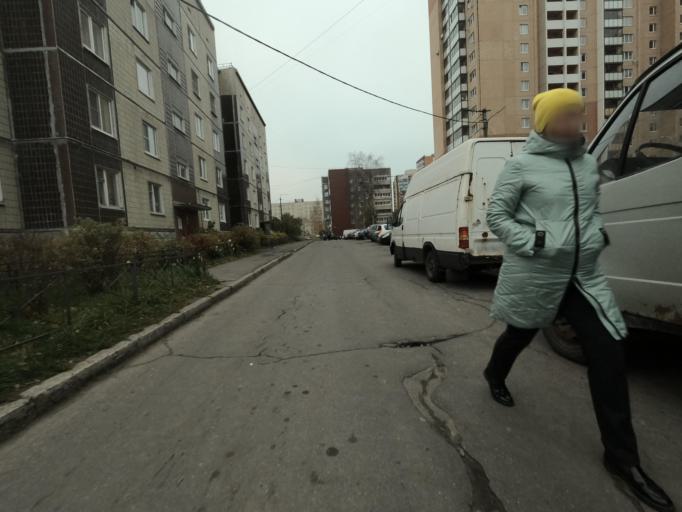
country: RU
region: Leningrad
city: Kirovsk
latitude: 59.8842
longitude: 30.9928
